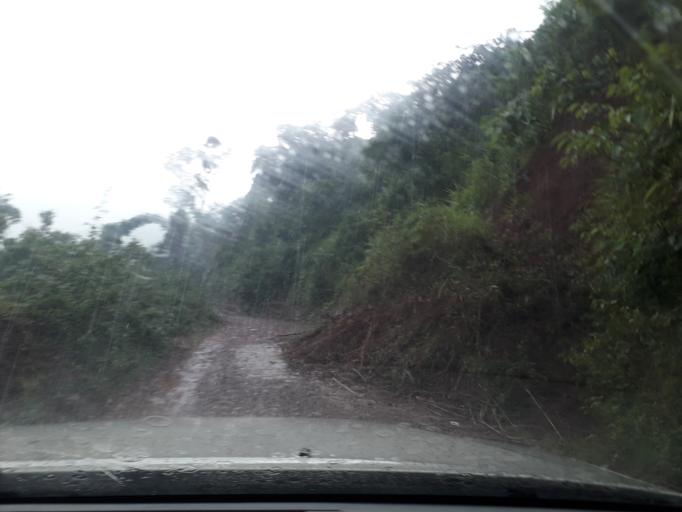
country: LA
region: Oudomxai
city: Muang La
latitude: 21.2483
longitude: 102.0043
